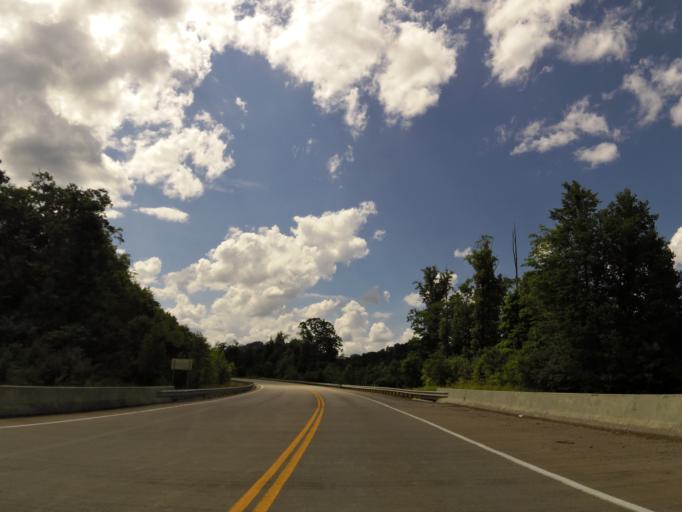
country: US
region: Kentucky
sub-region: Harlan County
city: Harlan
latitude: 36.7890
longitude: -83.2505
